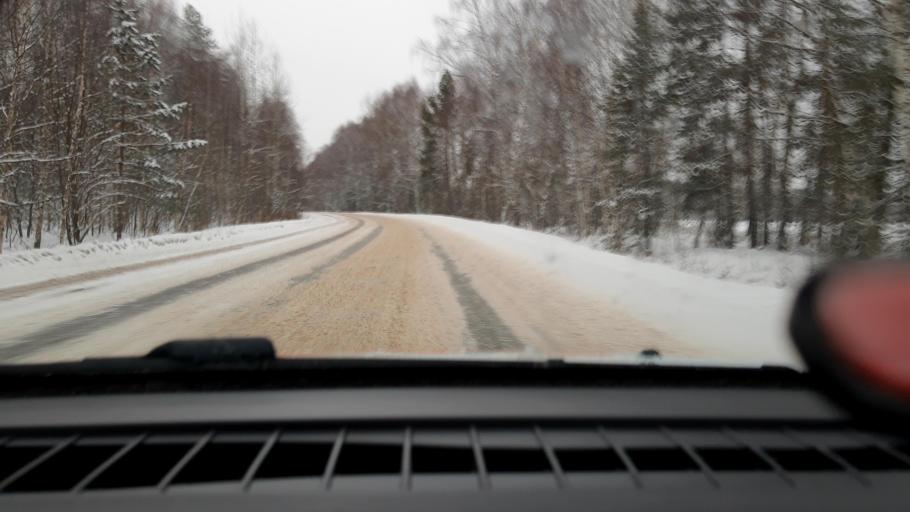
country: RU
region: Nizjnij Novgorod
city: Pamyat' Parizhskoy Kommuny
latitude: 56.2550
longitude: 44.4685
